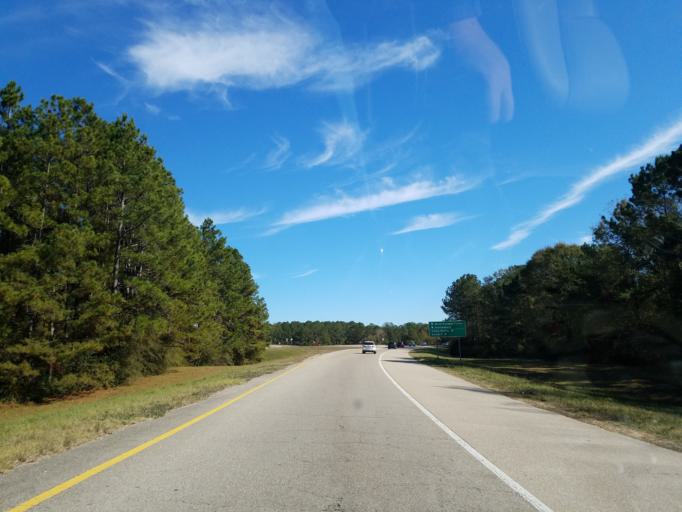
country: US
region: Mississippi
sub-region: Forrest County
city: Hattiesburg
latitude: 31.2430
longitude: -89.2788
